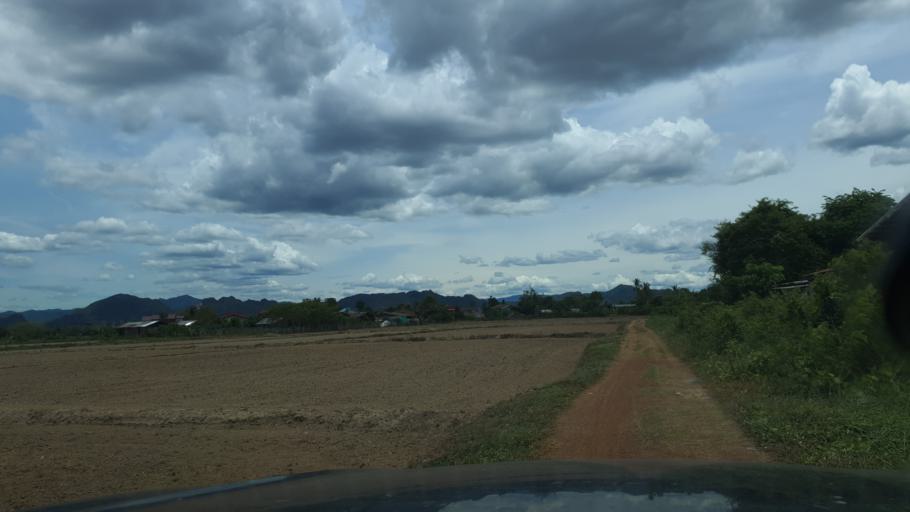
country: TH
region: Sukhothai
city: Thung Saliam
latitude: 17.3129
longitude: 99.5691
